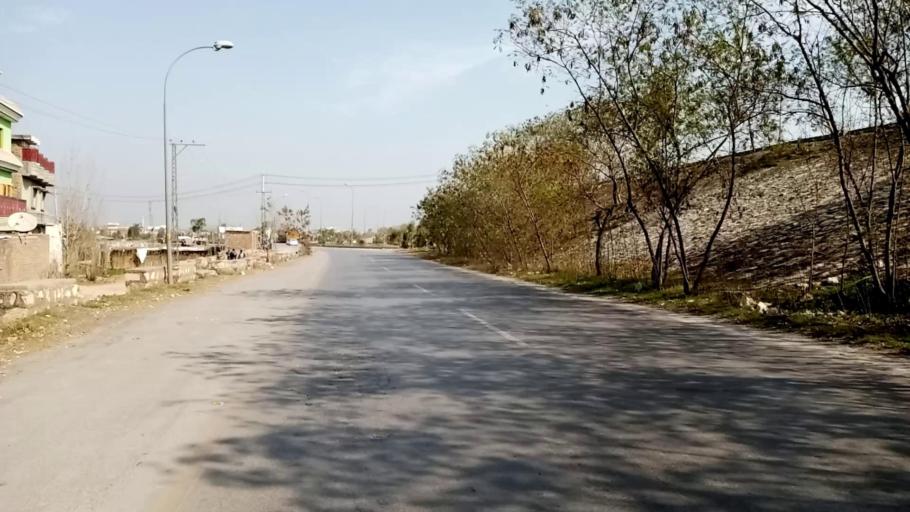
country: PK
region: Khyber Pakhtunkhwa
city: Peshawar
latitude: 34.0264
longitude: 71.6426
